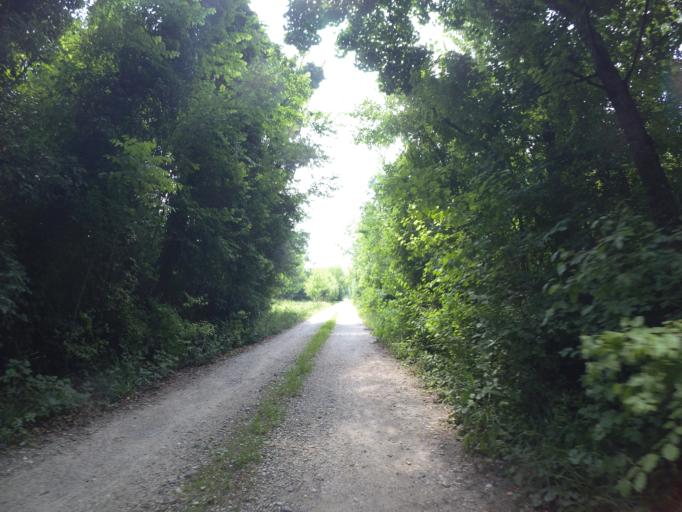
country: IT
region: Friuli Venezia Giulia
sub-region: Provincia di Udine
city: Bertiolo
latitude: 45.9243
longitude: 13.0418
